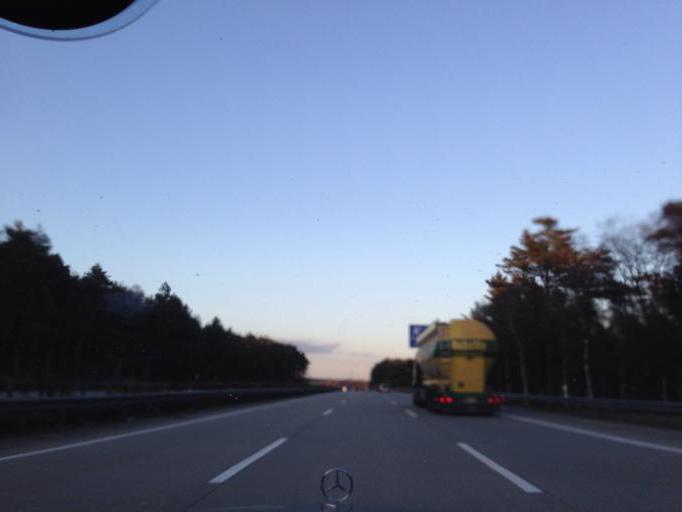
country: DE
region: Lower Saxony
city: Egestorf
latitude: 53.1526
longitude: 10.0428
